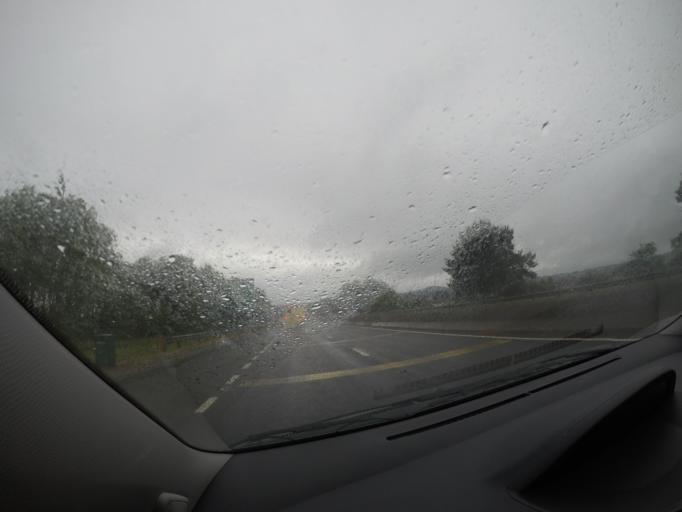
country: GB
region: Scotland
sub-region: Dundee City
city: Dundee
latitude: 56.4990
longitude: -2.9496
